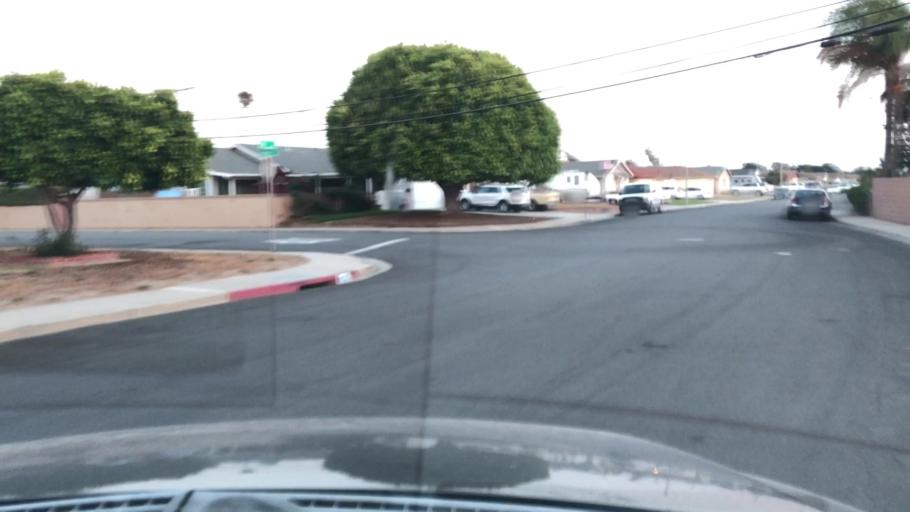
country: US
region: California
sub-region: Ventura County
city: Port Hueneme
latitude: 34.1655
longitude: -119.1880
